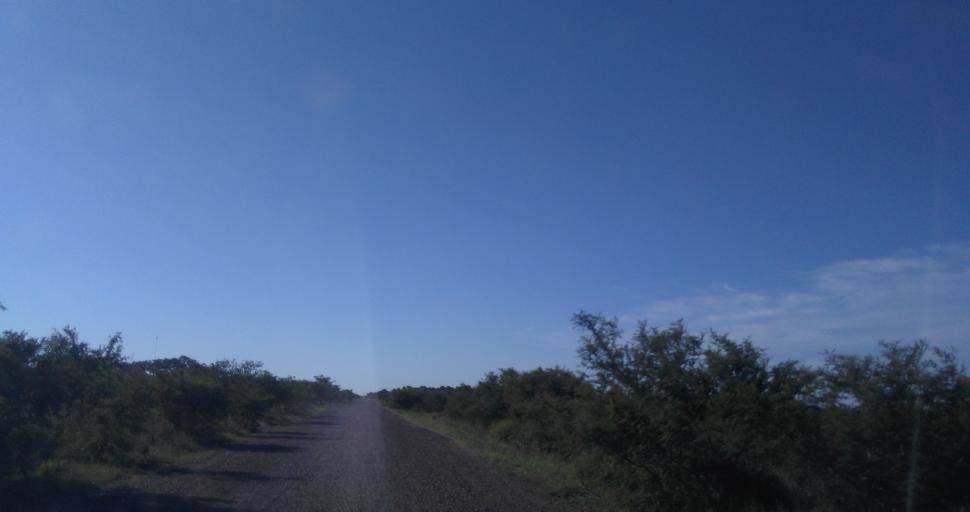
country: AR
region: Chaco
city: Barranqueras
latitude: -27.4235
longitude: -58.9313
